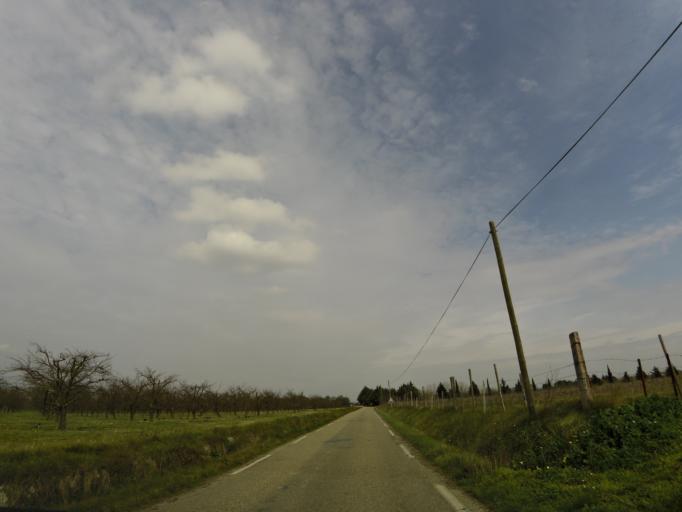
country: FR
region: Languedoc-Roussillon
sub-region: Departement de l'Herault
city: Marsillargues
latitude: 43.6748
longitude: 4.1872
